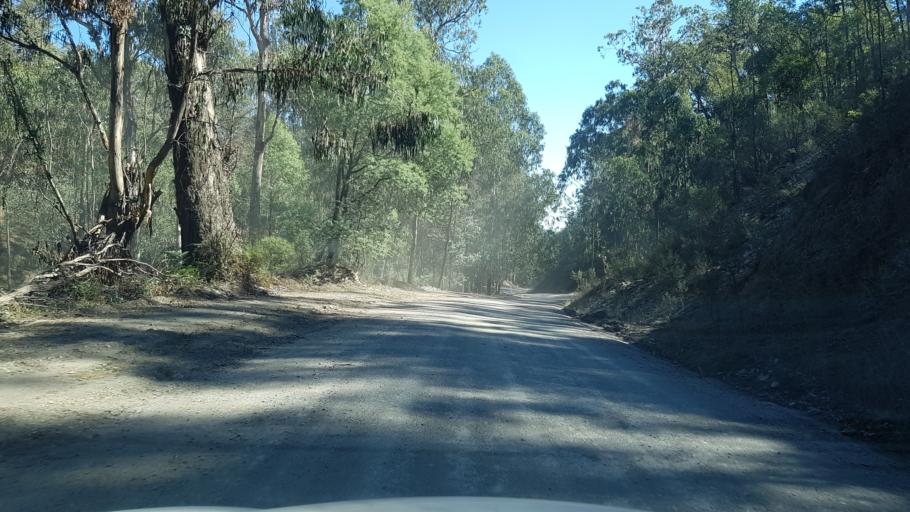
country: AU
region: Victoria
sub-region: Mansfield
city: Mansfield
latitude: -36.8365
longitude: 146.4964
